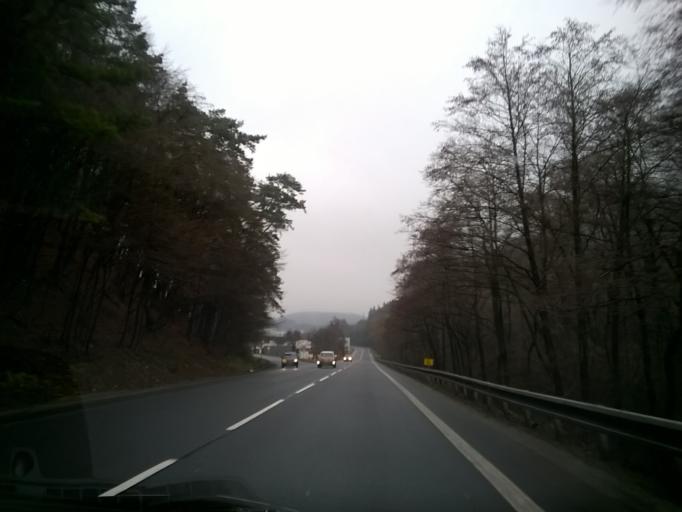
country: SK
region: Banskobystricky
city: Ziar nad Hronom
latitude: 48.5947
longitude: 18.8943
